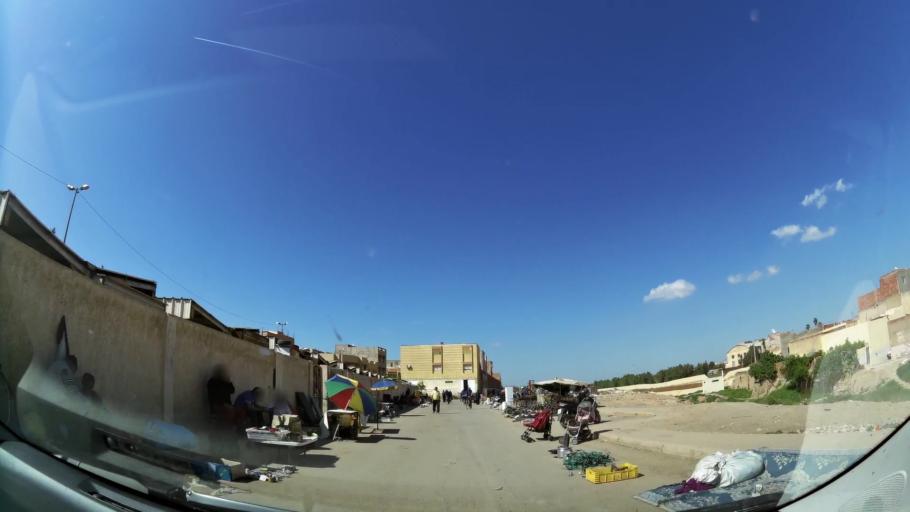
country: MA
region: Oriental
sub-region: Oujda-Angad
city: Oujda
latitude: 34.6841
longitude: -1.9293
